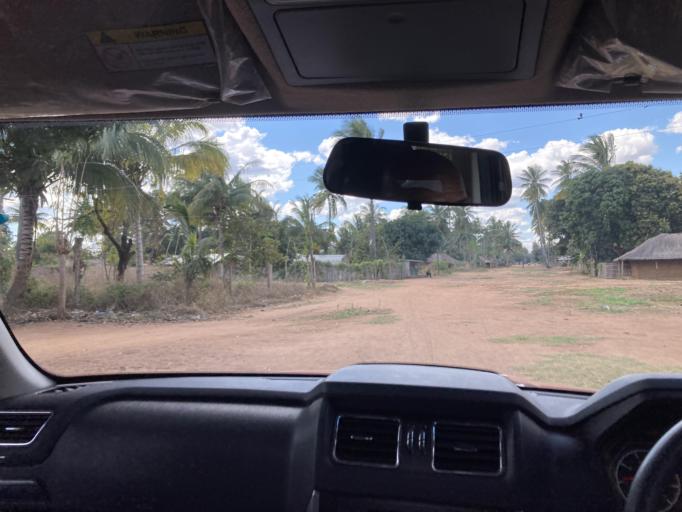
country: MZ
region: Cabo Delgado
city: Montepuez
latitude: -13.1435
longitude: 38.9969
